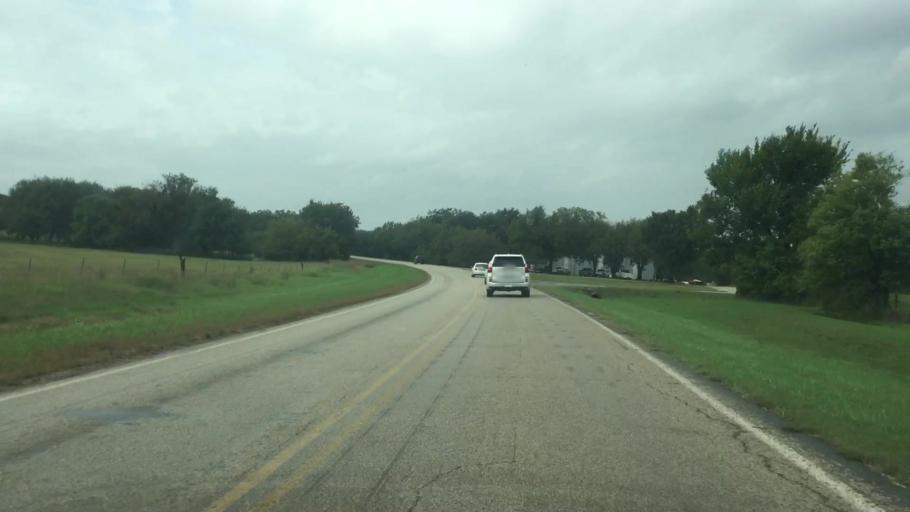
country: US
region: Kansas
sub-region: Allen County
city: Iola
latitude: 37.8855
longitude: -95.4288
